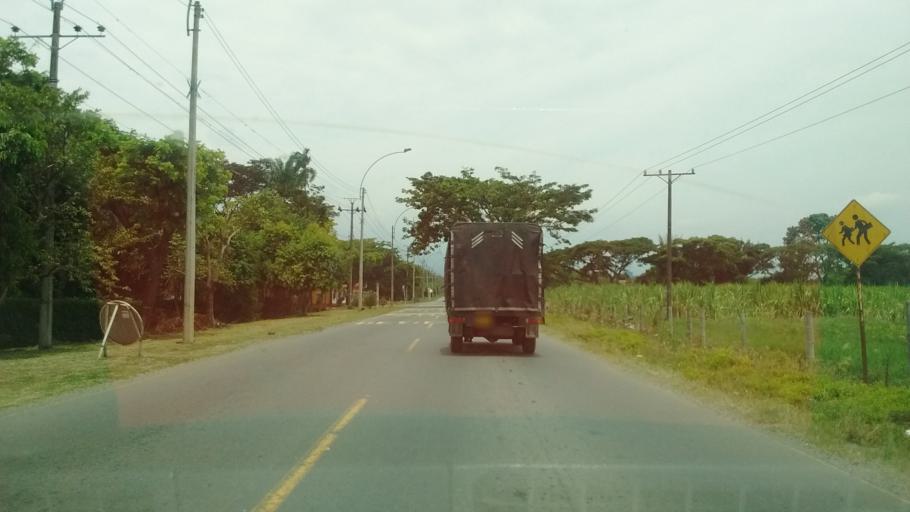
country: CO
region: Valle del Cauca
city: Jamundi
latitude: 3.3192
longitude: -76.4944
